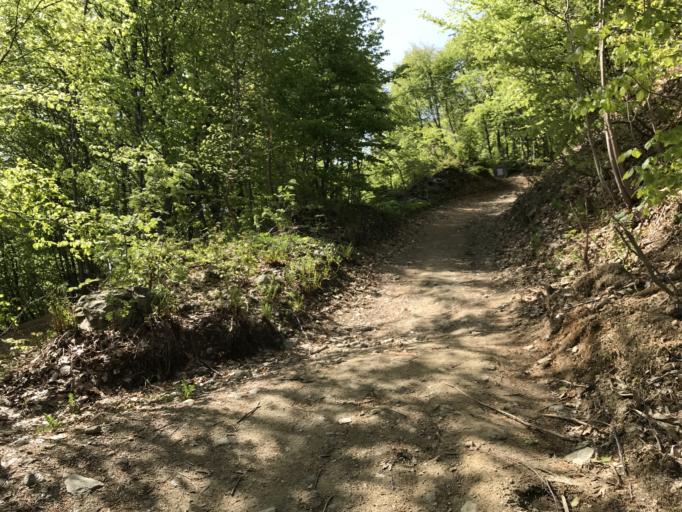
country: IT
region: Piedmont
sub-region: Provincia di Cuneo
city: Robilante
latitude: 44.2920
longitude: 7.5503
